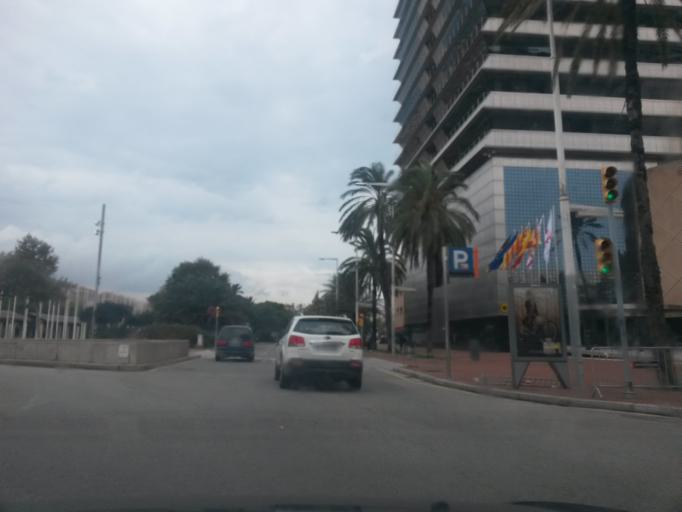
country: ES
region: Catalonia
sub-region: Provincia de Barcelona
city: Ciutat Vella
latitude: 41.3876
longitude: 2.1966
